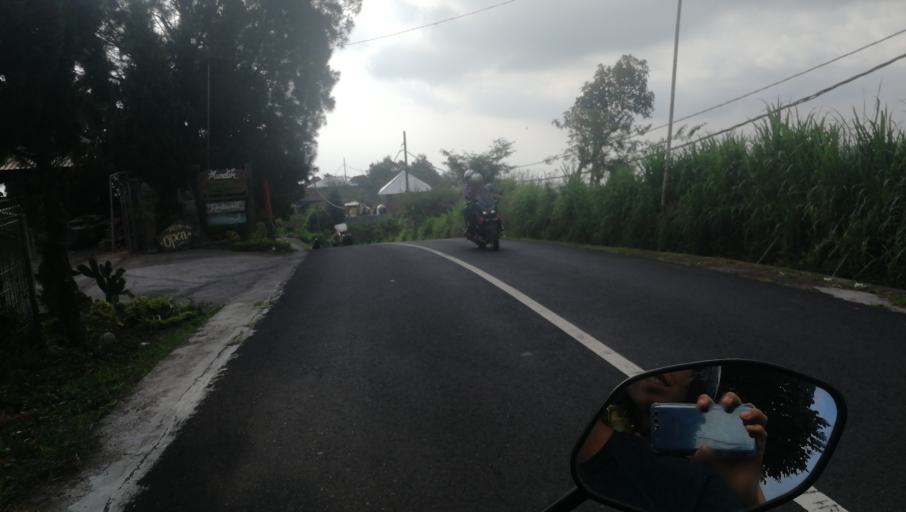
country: ID
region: Bali
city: Munduk
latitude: -8.2602
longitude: 115.0833
